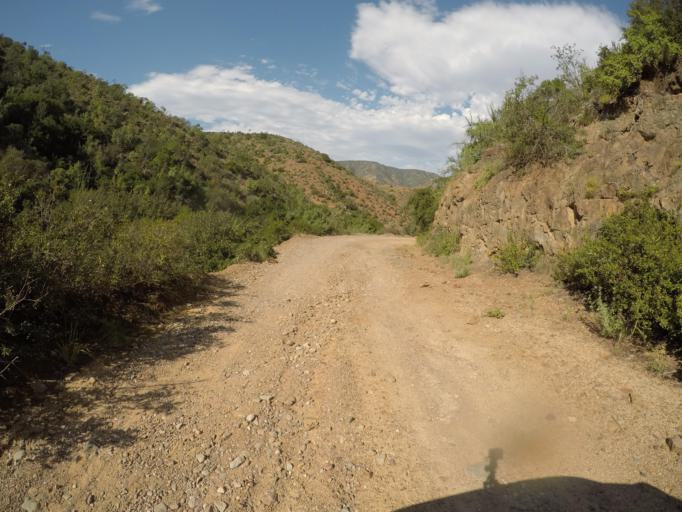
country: ZA
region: Eastern Cape
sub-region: Cacadu District Municipality
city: Kareedouw
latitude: -33.6569
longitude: 24.4011
